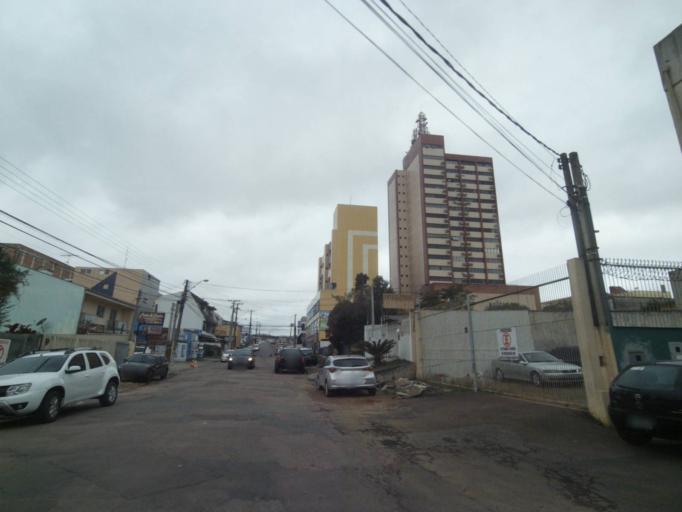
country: BR
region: Parana
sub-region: Sao Jose Dos Pinhais
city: Sao Jose dos Pinhais
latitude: -25.5169
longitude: -49.2969
